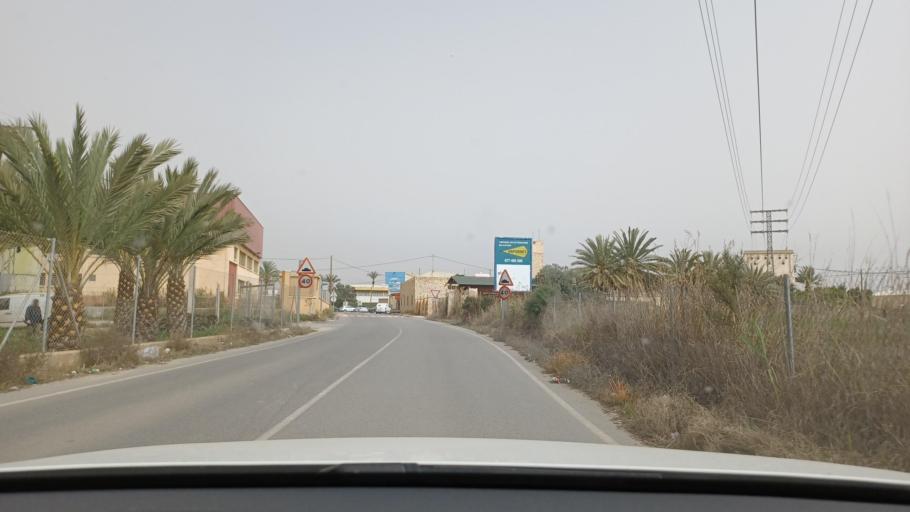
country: ES
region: Valencia
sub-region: Provincia de Alicante
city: Elche
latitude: 38.2492
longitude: -0.6915
